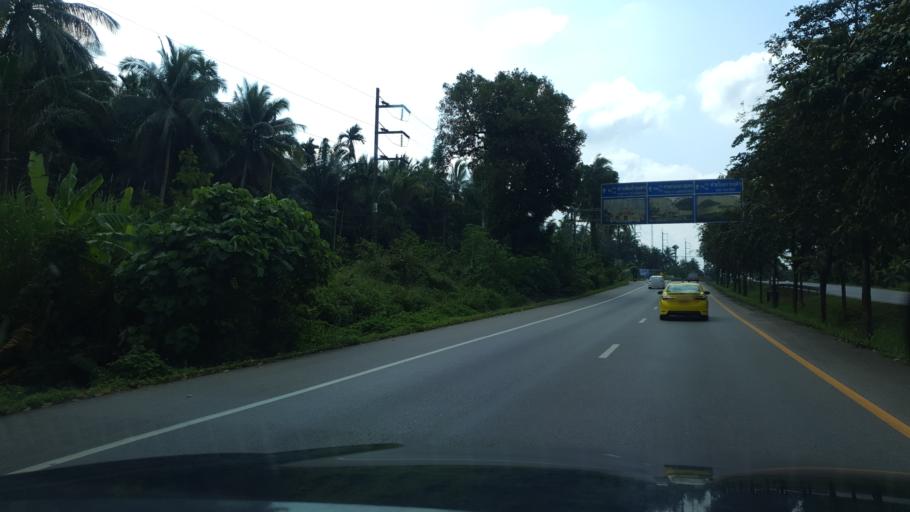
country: TH
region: Chumphon
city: Tha Sae
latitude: 10.6228
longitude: 99.1765
